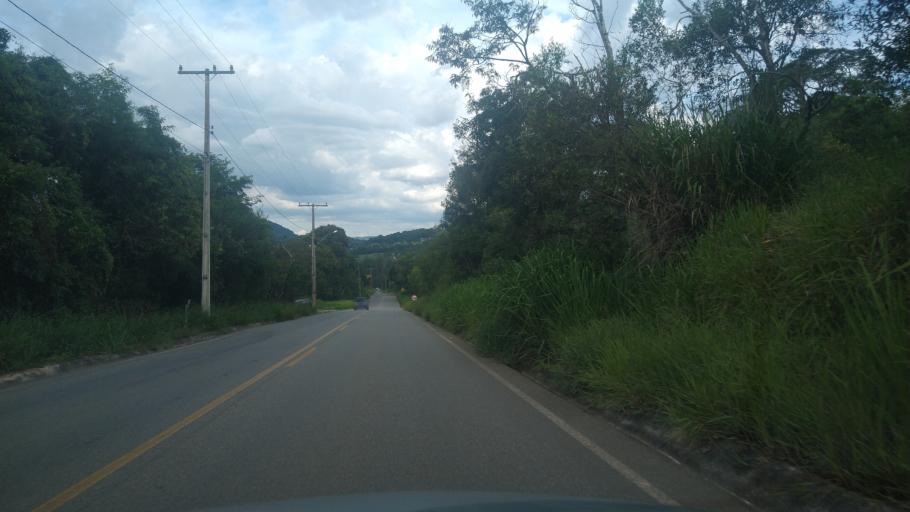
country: BR
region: Minas Gerais
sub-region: Extrema
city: Extrema
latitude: -22.8078
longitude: -46.3078
